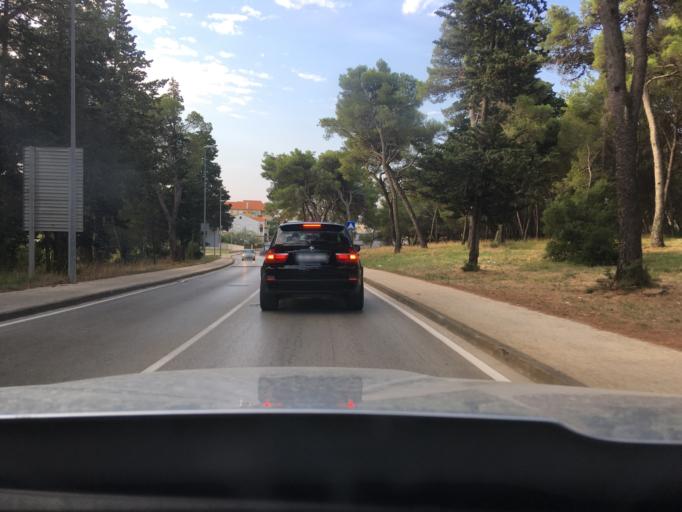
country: HR
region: Zadarska
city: Zadar
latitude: 44.1380
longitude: 15.2288
